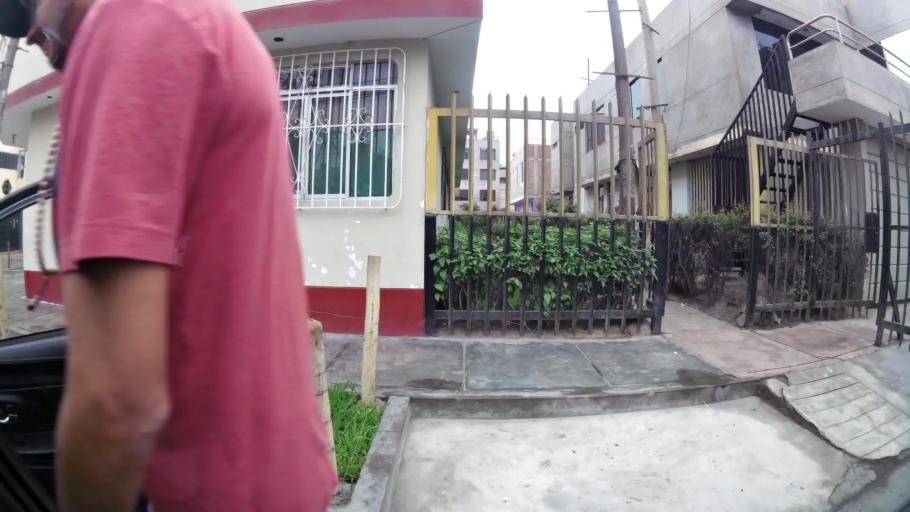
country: PE
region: Lima
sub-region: Lima
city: Independencia
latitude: -11.9683
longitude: -77.0742
